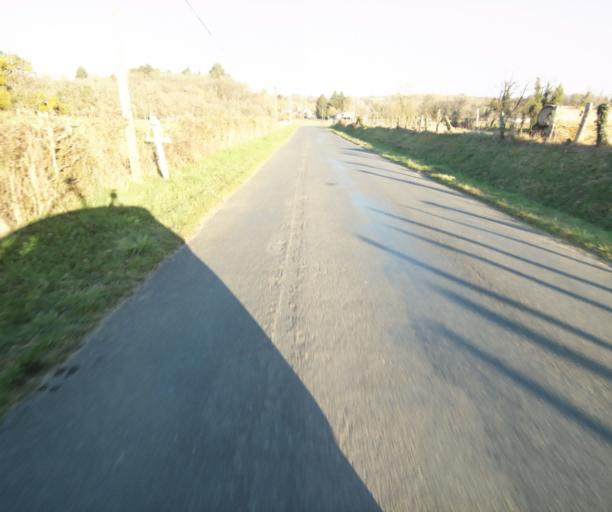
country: FR
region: Limousin
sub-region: Departement de la Correze
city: Saint-Clement
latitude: 45.3514
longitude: 1.6420
